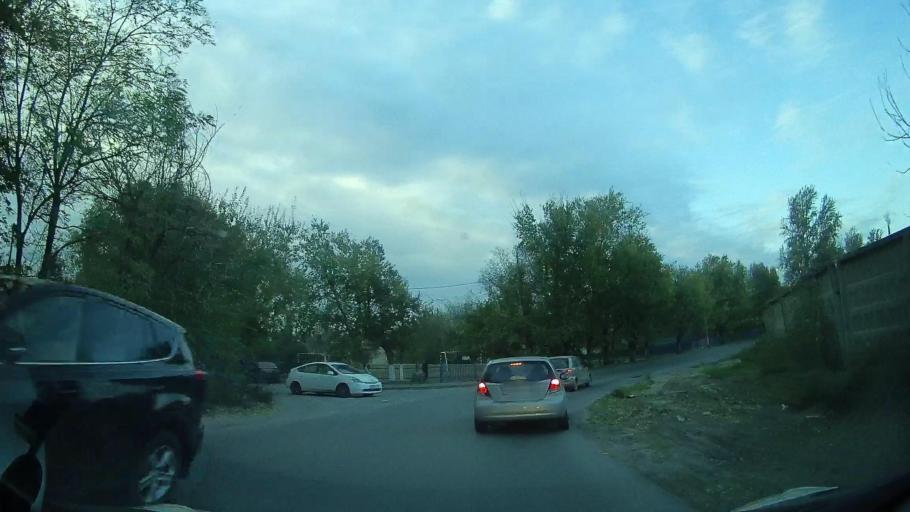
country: RU
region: Rostov
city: Severnyy
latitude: 47.2633
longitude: 39.6466
